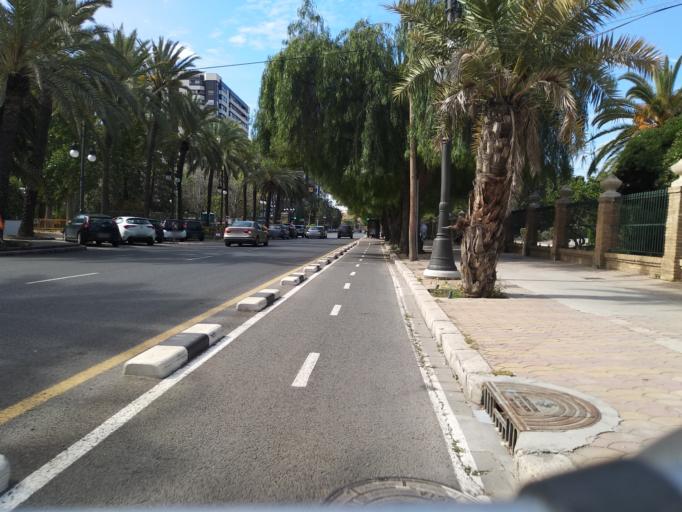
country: ES
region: Valencia
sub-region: Provincia de Valencia
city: Valencia
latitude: 39.4804
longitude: -0.3659
